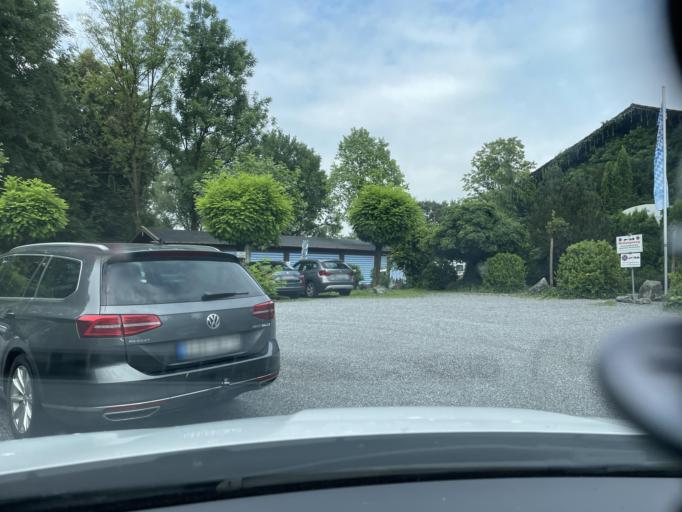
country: DE
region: Bavaria
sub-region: Upper Bavaria
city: Schechen
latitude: 47.9248
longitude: 12.1346
